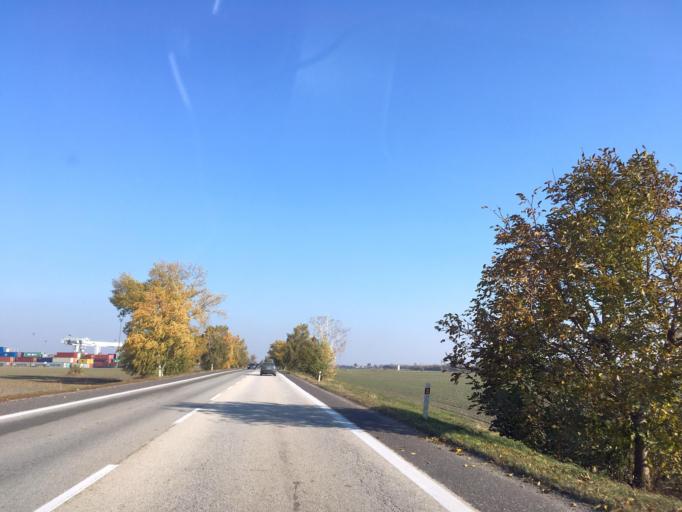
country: SK
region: Trnavsky
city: Dunajska Streda
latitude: 47.9770
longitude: 17.6217
